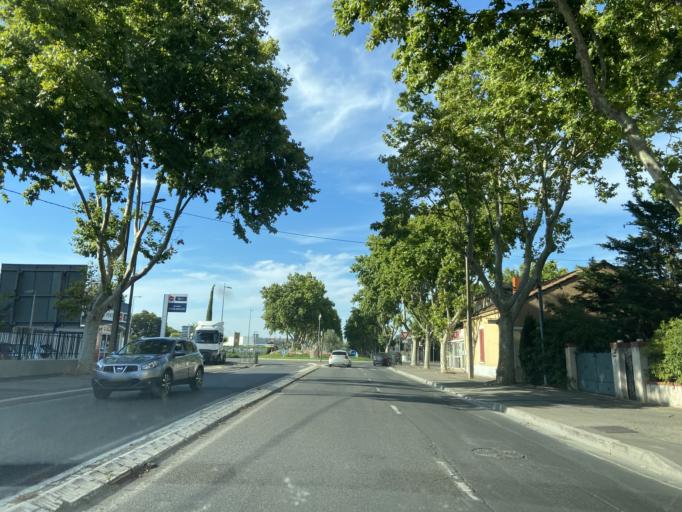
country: FR
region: Provence-Alpes-Cote d'Azur
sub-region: Departement des Bouches-du-Rhone
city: Miramas
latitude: 43.5869
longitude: 5.0026
